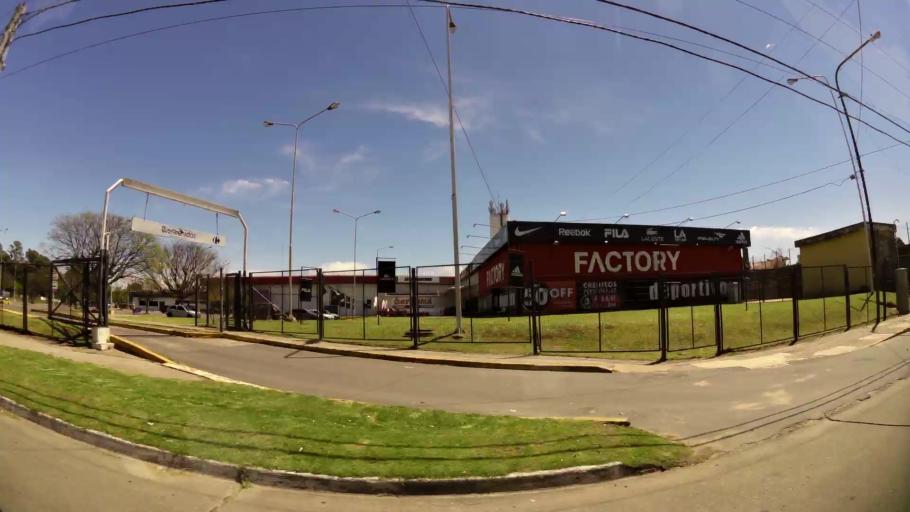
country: AR
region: Buenos Aires
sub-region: Partido de Quilmes
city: Quilmes
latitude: -34.7359
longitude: -58.2763
